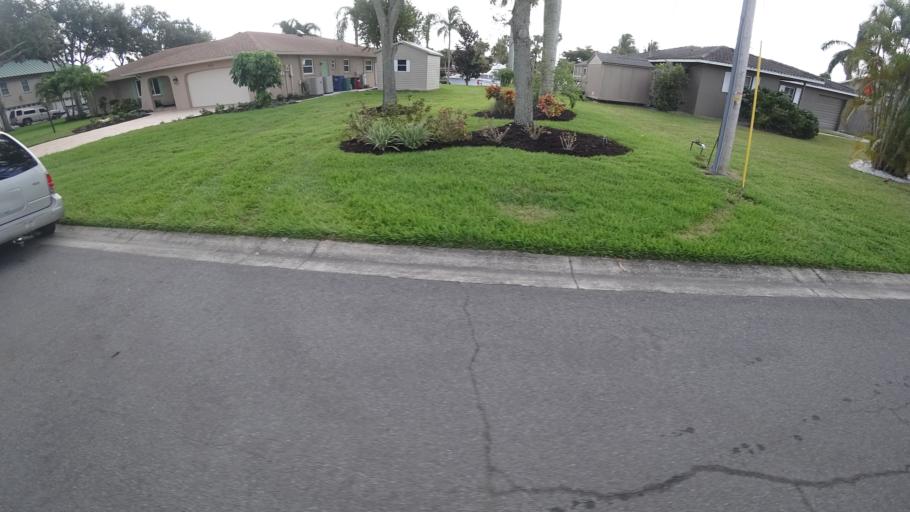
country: US
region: Florida
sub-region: Manatee County
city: Memphis
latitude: 27.5605
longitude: -82.5702
